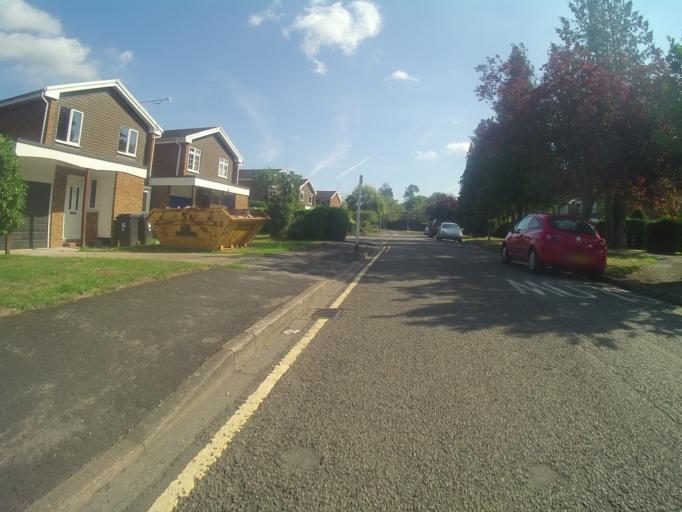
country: GB
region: England
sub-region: Surrey
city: Woking
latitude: 51.3154
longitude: -0.5760
